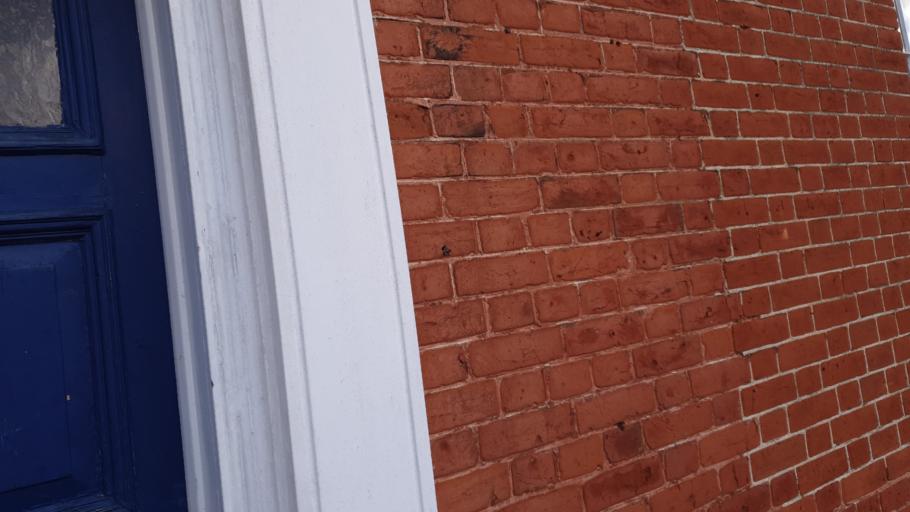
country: GB
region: England
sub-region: Suffolk
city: Hadleigh
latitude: 52.0419
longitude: 0.9554
